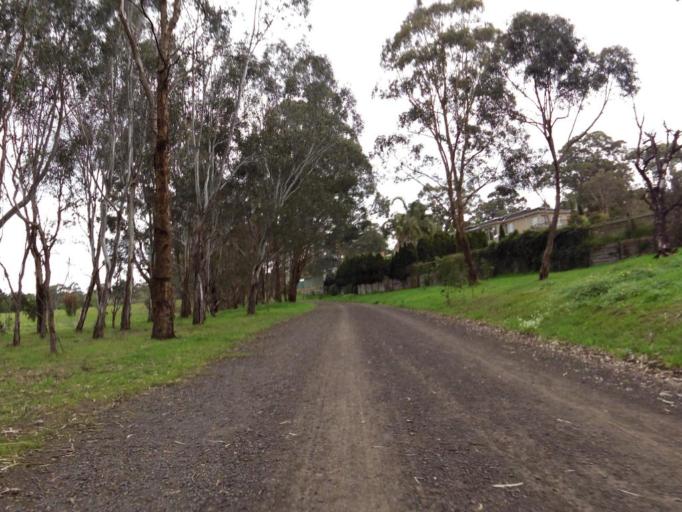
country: AU
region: Victoria
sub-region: Nillumbik
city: Eltham
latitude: -37.7428
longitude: 145.1632
